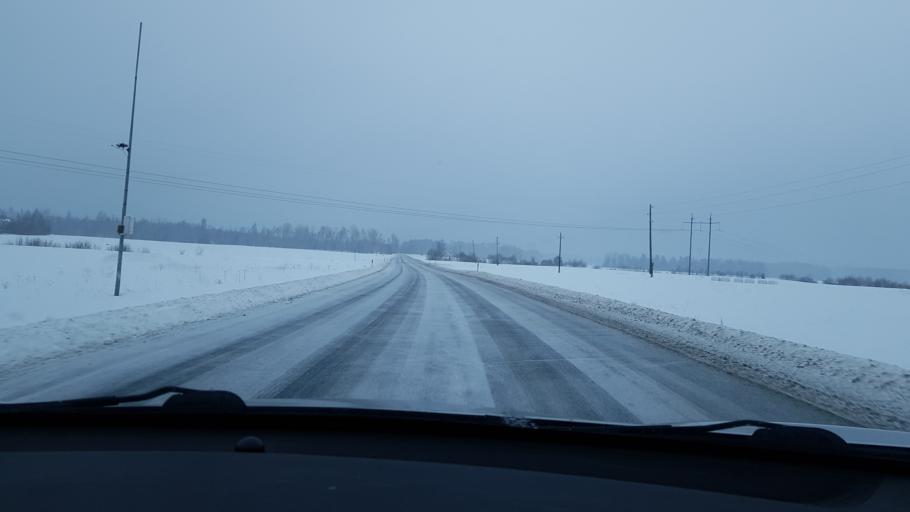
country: EE
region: Jaervamaa
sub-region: Tueri vald
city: Sarevere
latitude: 58.7312
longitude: 25.2880
